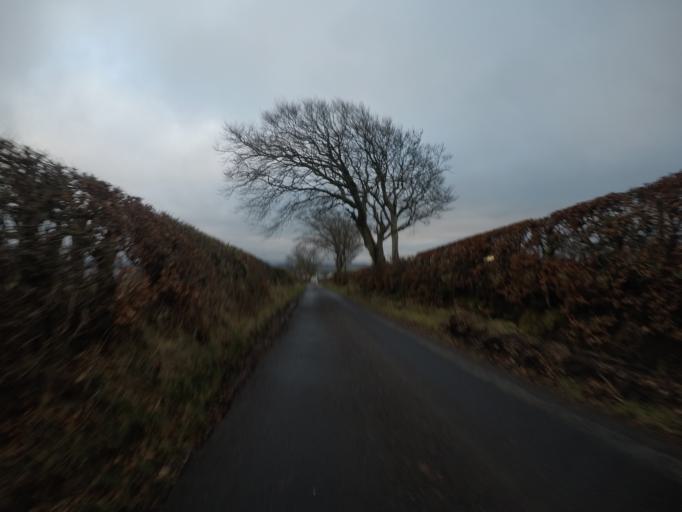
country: GB
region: Scotland
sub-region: North Ayrshire
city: Dalry
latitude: 55.7217
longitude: -4.7610
